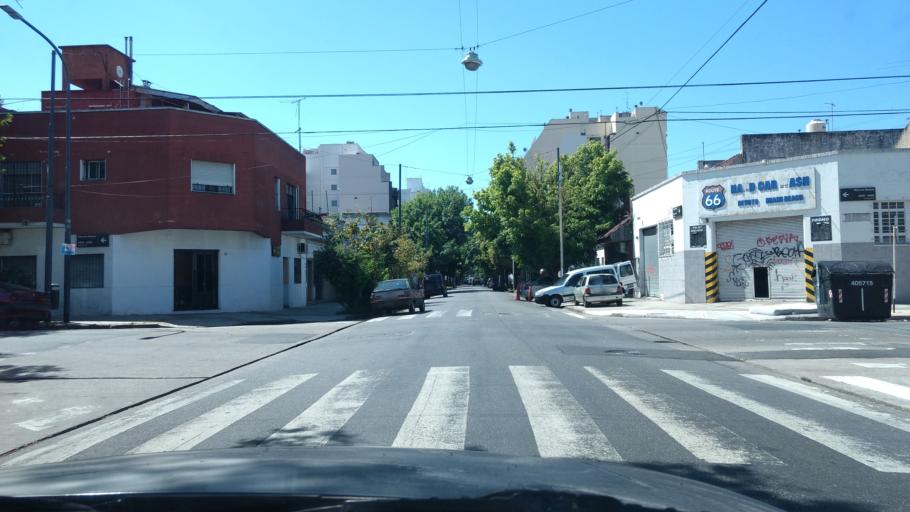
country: AR
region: Buenos Aires F.D.
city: Villa Santa Rita
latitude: -34.6140
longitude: -58.5064
